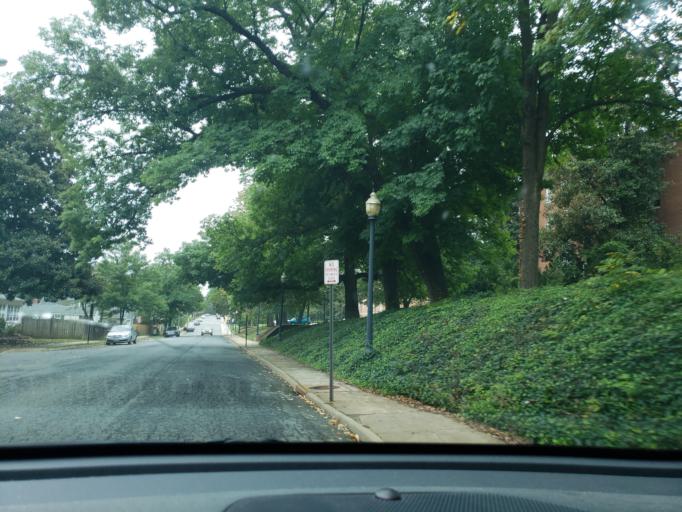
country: US
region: Virginia
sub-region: City of Fredericksburg
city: Fredericksburg
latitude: 38.3011
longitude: -77.4716
